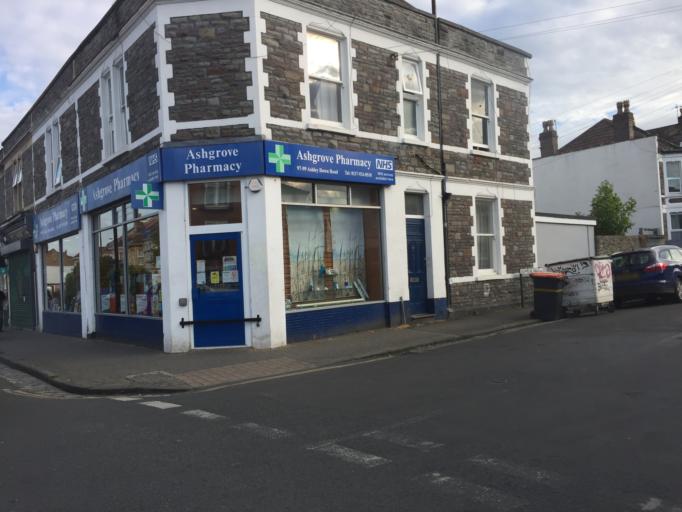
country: GB
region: England
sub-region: Bristol
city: Bristol
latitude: 51.4813
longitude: -2.5828
